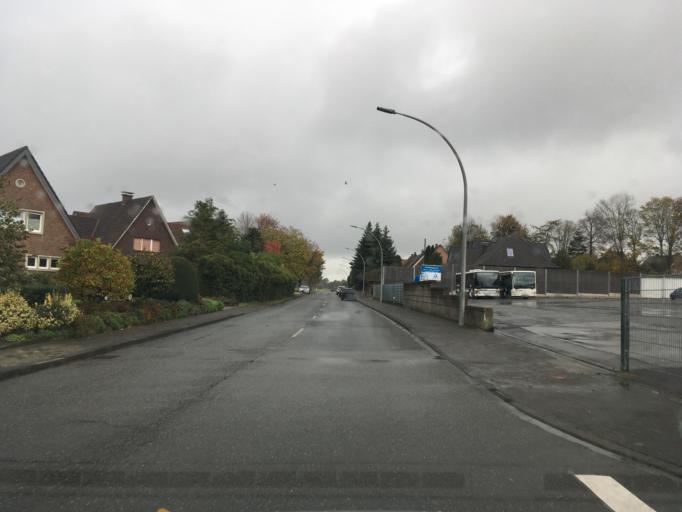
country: DE
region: North Rhine-Westphalia
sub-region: Regierungsbezirk Munster
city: Klein Reken
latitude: 51.8338
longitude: 7.0391
